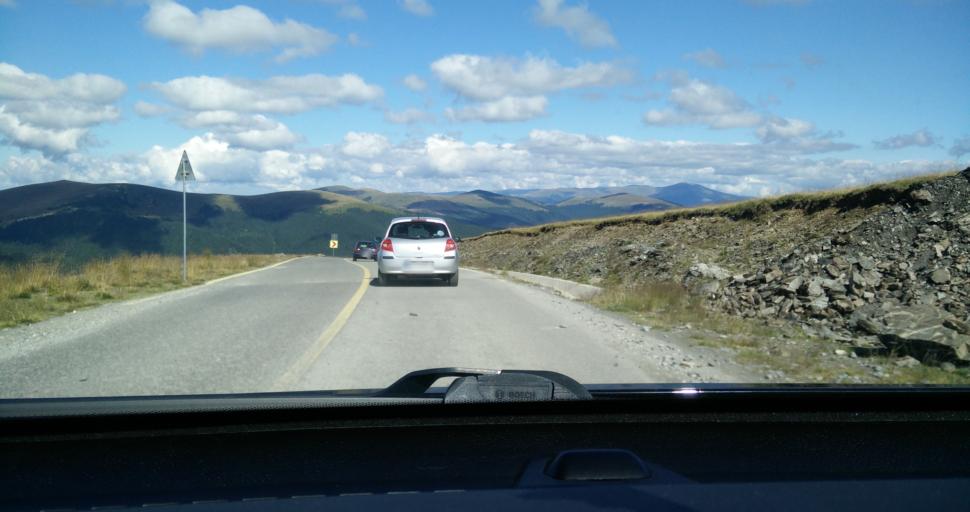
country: RO
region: Gorj
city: Novaci-Straini
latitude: 45.3768
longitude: 23.6530
